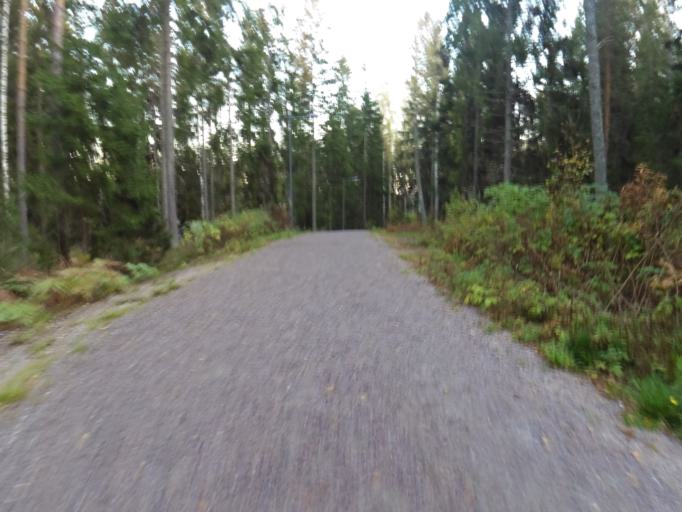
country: FI
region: Uusimaa
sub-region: Helsinki
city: Kauniainen
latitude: 60.2793
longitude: 24.7358
